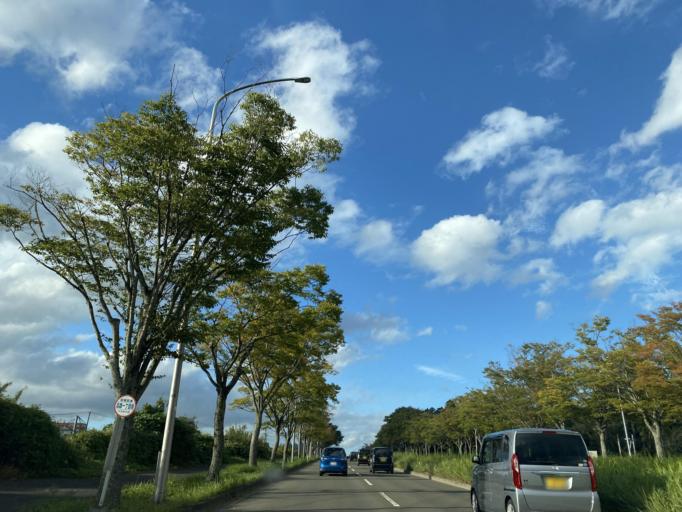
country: JP
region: Miyagi
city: Sendai-shi
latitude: 38.3309
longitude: 140.8407
